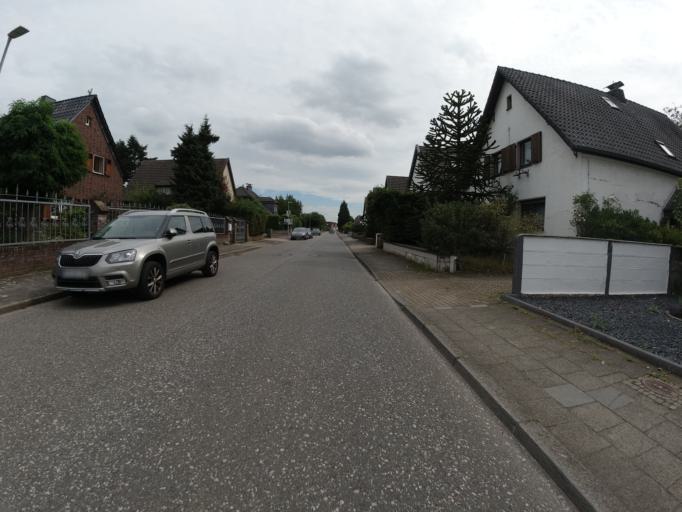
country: DE
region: North Rhine-Westphalia
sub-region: Regierungsbezirk Dusseldorf
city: Moers
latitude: 51.4667
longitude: 6.6554
